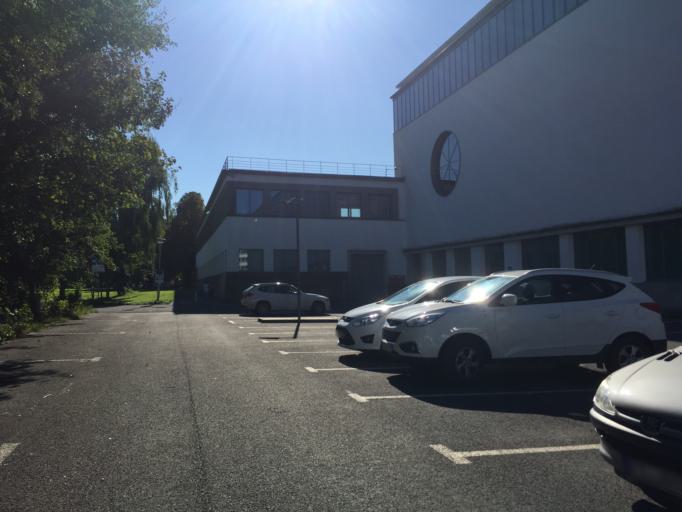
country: DE
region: Saxony
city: Dresden
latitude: 51.0450
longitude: 13.7463
